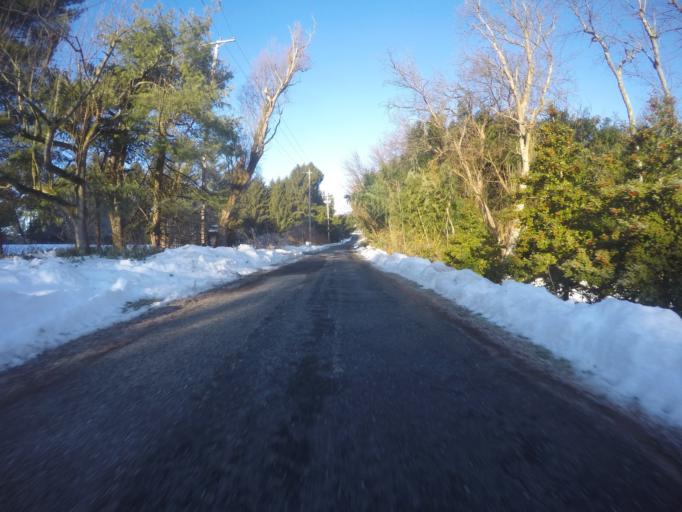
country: US
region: Maryland
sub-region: Baltimore County
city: Hunt Valley
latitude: 39.5471
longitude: -76.6701
